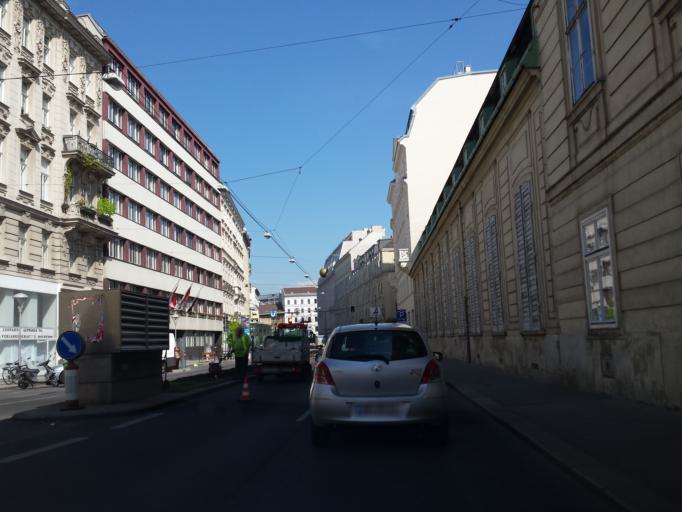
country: AT
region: Vienna
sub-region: Wien Stadt
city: Vienna
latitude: 48.1939
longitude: 16.3704
